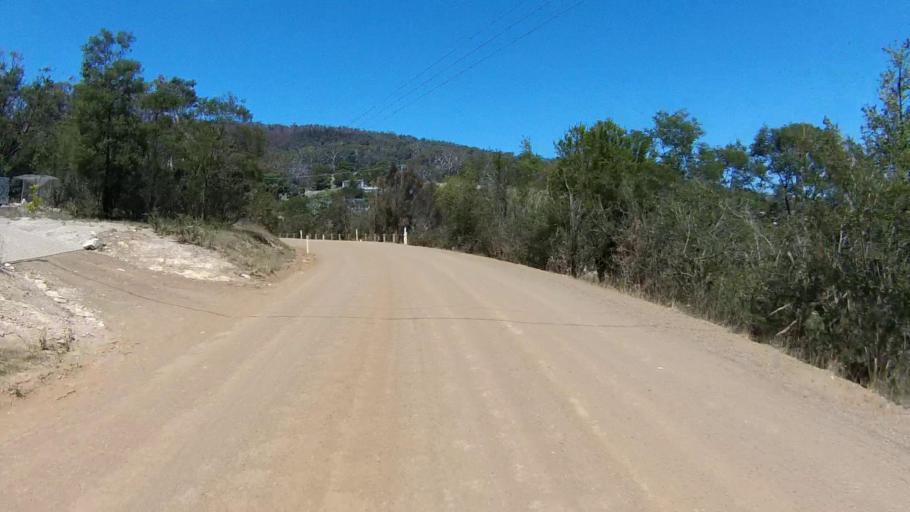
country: AU
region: Tasmania
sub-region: Clarence
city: Lauderdale
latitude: -42.9307
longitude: 147.4658
